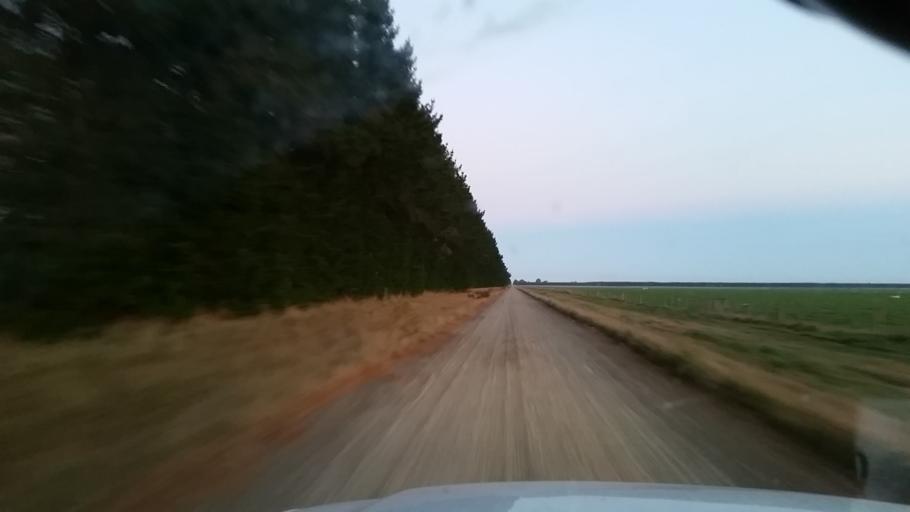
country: NZ
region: Canterbury
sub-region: Ashburton District
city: Tinwald
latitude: -43.9477
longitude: 171.6129
